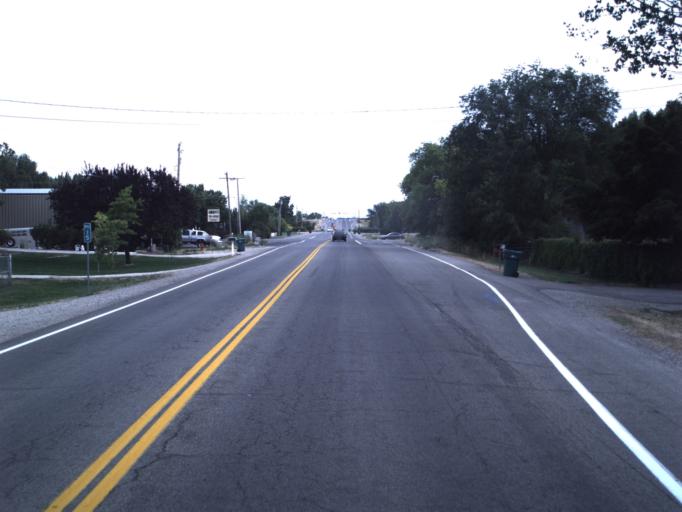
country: US
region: Utah
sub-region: Weber County
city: Marriott-Slaterville
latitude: 41.2531
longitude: -112.0252
